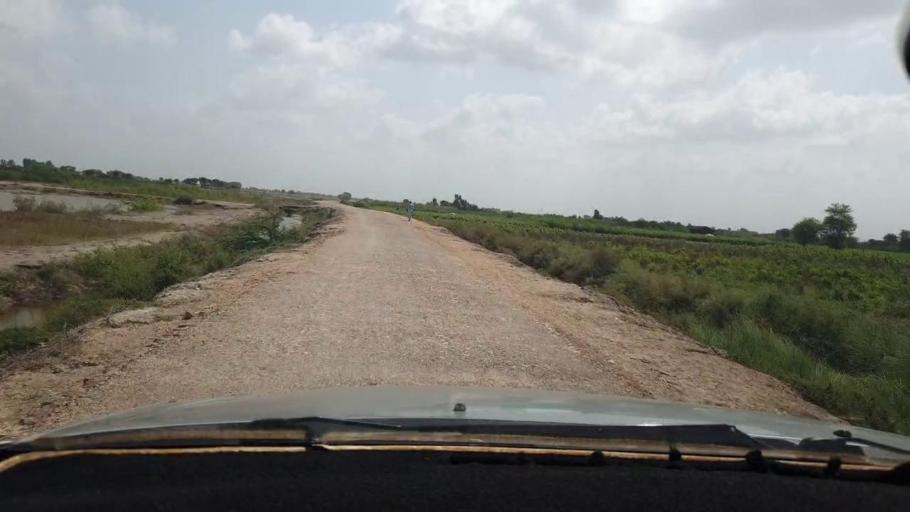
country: PK
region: Sindh
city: Tando Bago
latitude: 24.7206
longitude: 69.1728
